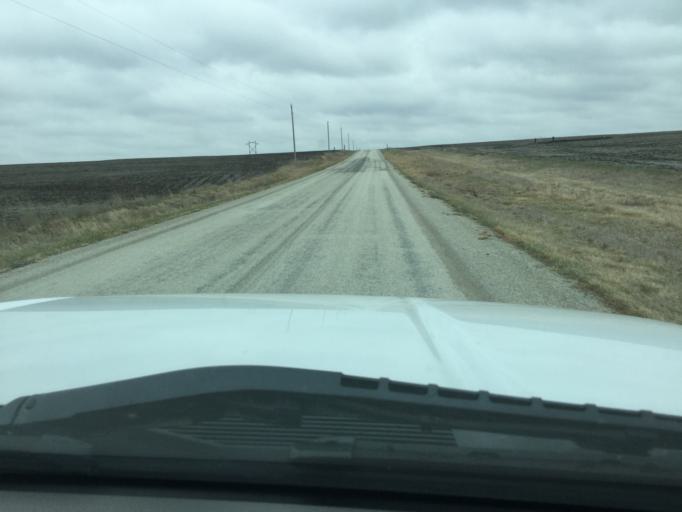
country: US
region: Kansas
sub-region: Nemaha County
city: Sabetha
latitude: 39.7981
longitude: -95.7821
